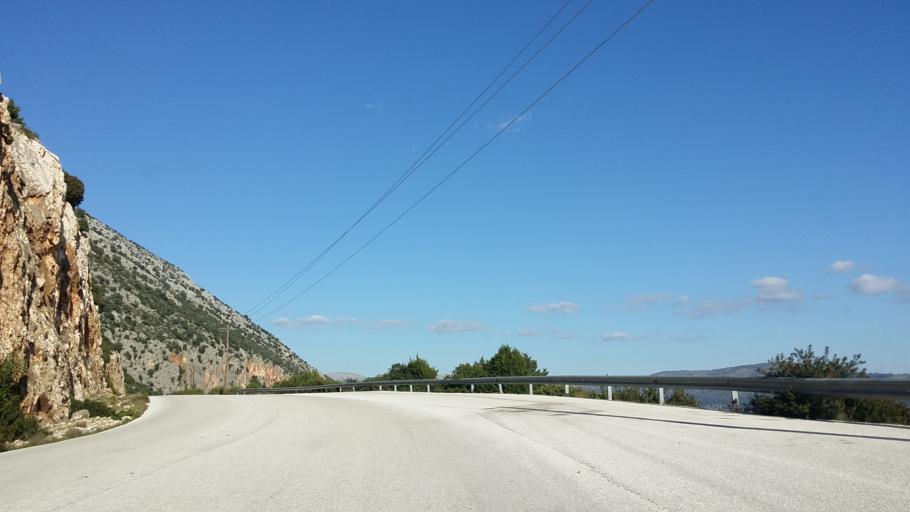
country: GR
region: West Greece
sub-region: Nomos Aitolias kai Akarnanias
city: Astakos
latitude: 38.5069
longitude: 21.0462
